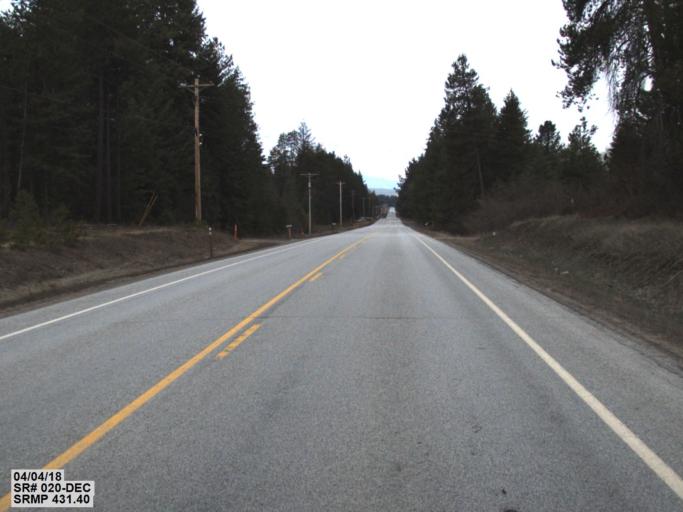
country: US
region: Washington
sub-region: Pend Oreille County
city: Newport
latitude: 48.2256
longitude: -117.1325
